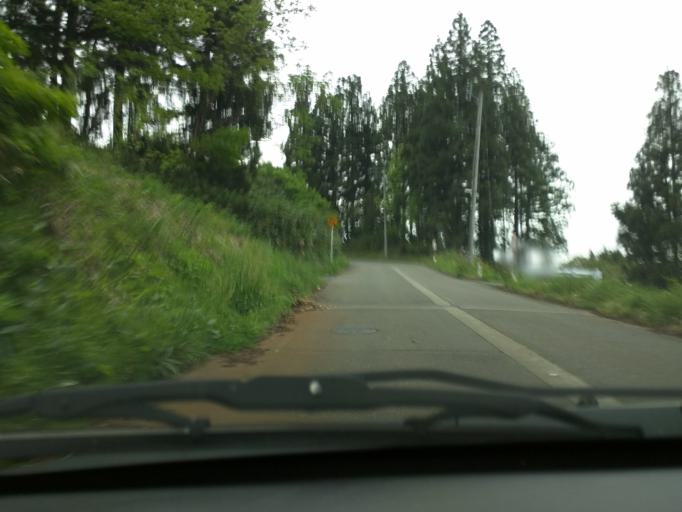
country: JP
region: Niigata
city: Muikamachi
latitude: 37.2221
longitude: 138.9516
